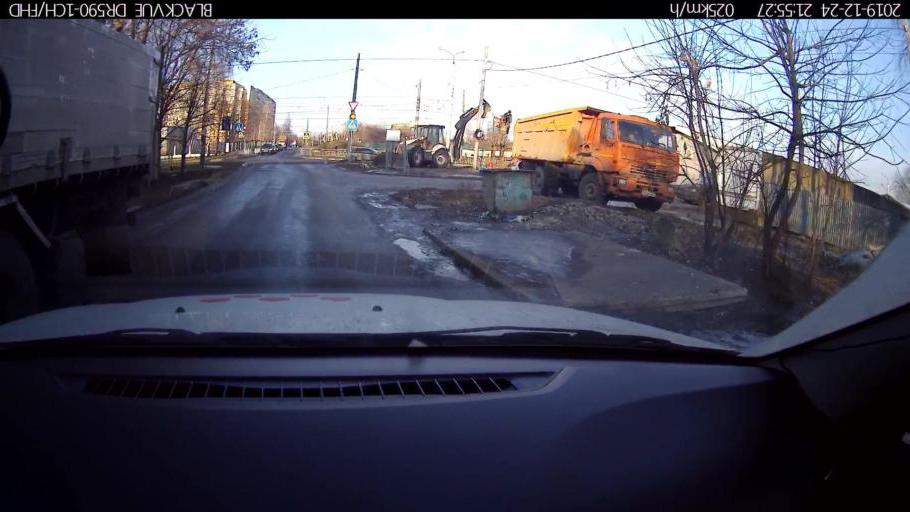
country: RU
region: Nizjnij Novgorod
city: Burevestnik
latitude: 56.2185
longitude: 43.8436
